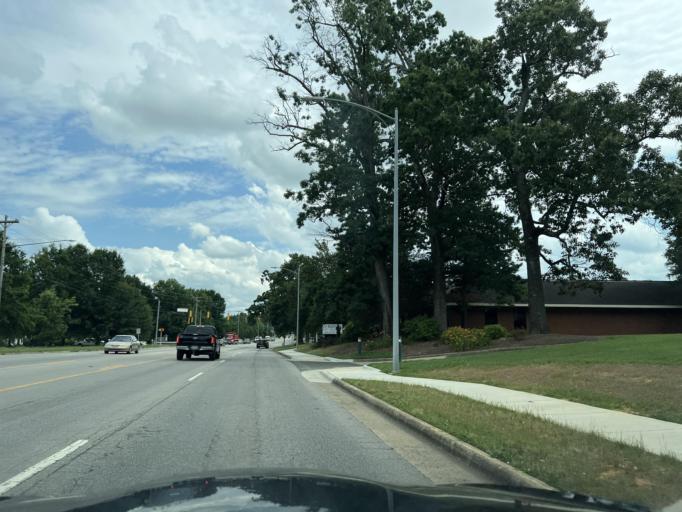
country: US
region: North Carolina
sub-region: Durham County
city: Durham
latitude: 36.0438
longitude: -78.9015
